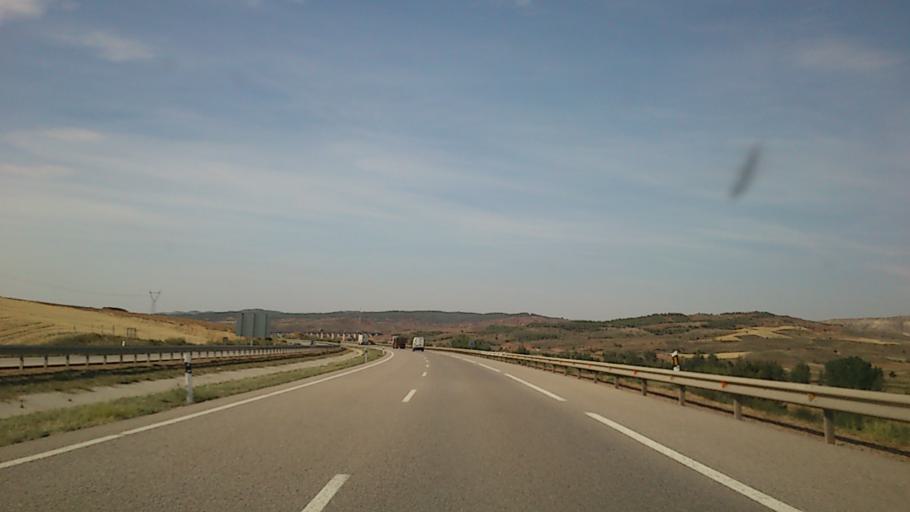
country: ES
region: Aragon
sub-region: Provincia de Teruel
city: Calamocha
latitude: 40.9296
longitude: -1.2665
